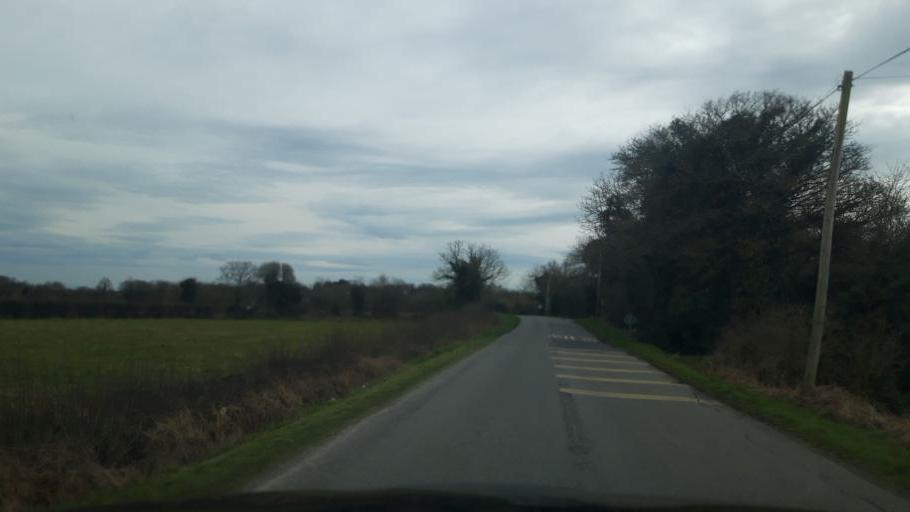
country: IE
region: Leinster
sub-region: Uibh Fhaili
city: Edenderry
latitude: 53.3274
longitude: -7.0356
